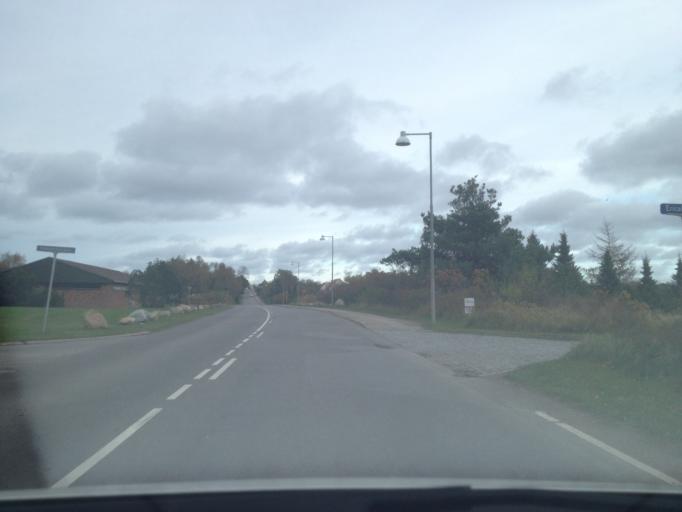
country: DK
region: Zealand
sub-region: Odsherred Kommune
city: Hojby
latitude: 55.9078
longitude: 11.5854
